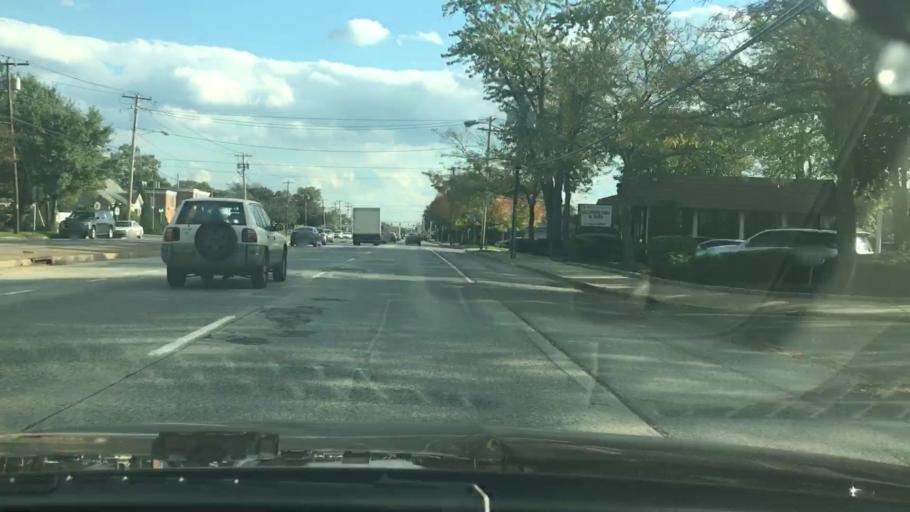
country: US
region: New York
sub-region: Suffolk County
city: Deer Park
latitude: 40.7689
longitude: -73.3324
